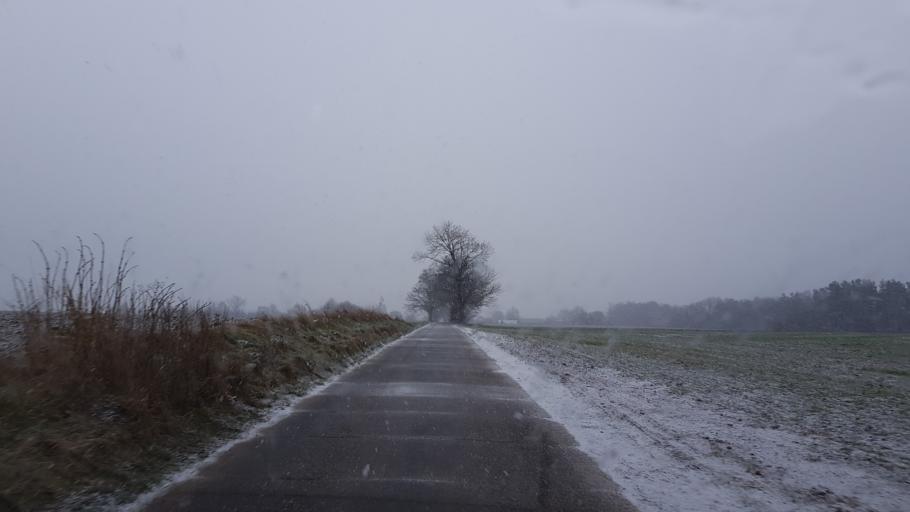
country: PL
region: West Pomeranian Voivodeship
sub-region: Powiat slawienski
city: Slawno
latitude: 54.2766
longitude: 16.6252
